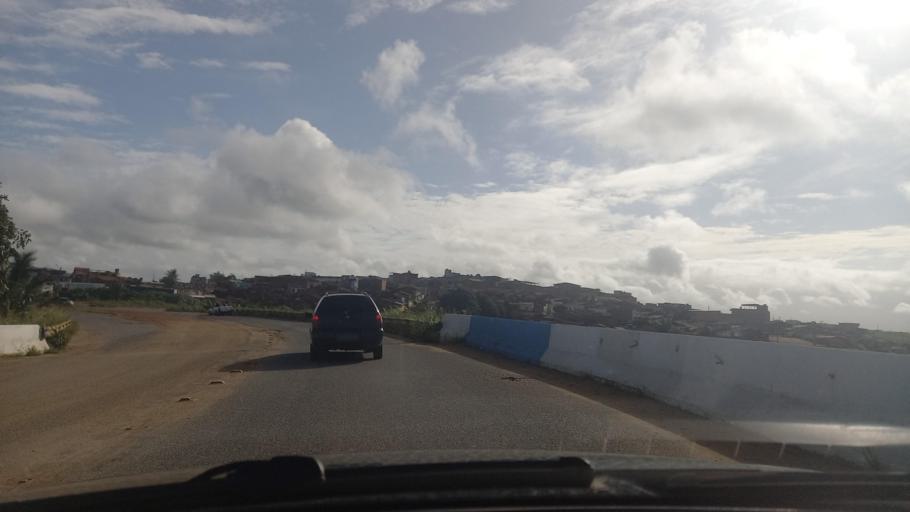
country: BR
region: Pernambuco
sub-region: Vitoria De Santo Antao
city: Vitoria de Santo Antao
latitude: -8.1279
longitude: -35.2821
